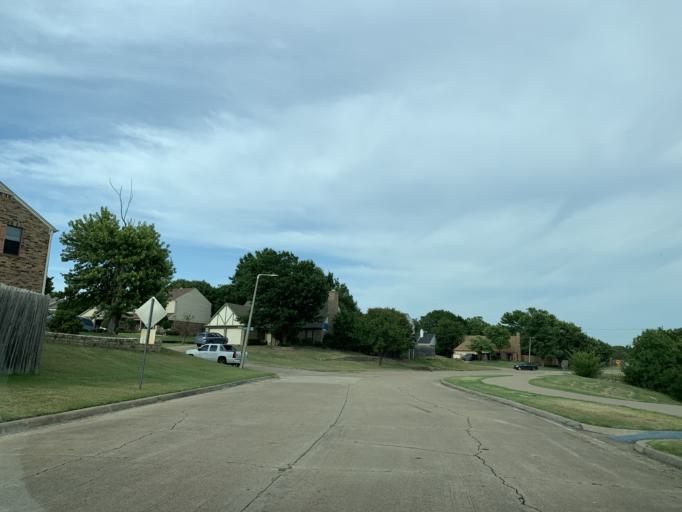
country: US
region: Texas
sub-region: Dallas County
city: Grand Prairie
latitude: 32.6601
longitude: -97.0449
